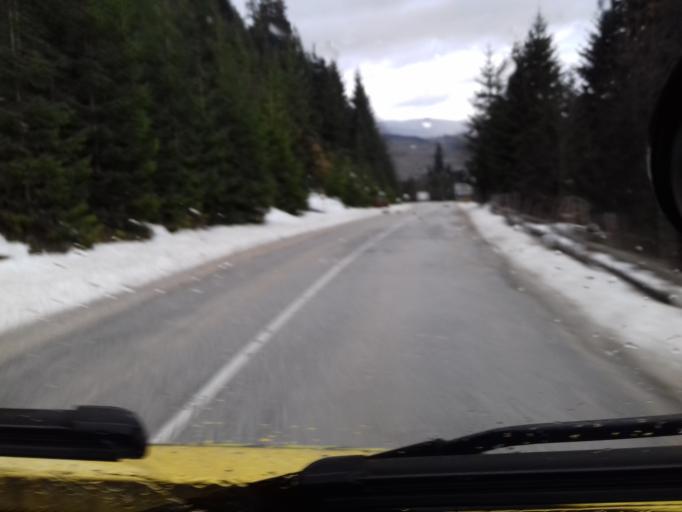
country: BA
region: Federation of Bosnia and Herzegovina
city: Turbe
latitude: 44.3154
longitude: 17.5167
